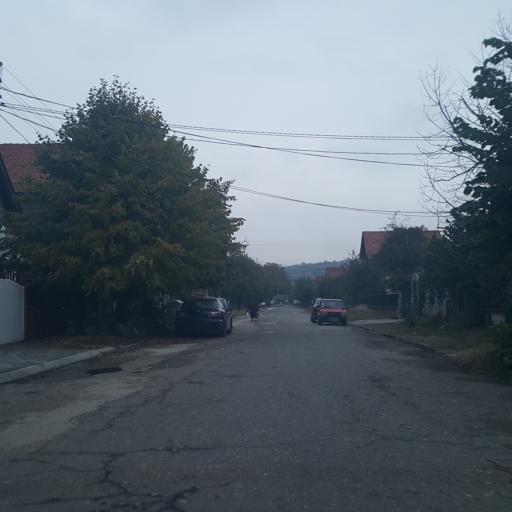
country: RS
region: Central Serbia
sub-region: Zajecarski Okrug
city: Zajecar
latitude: 43.9057
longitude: 22.2599
